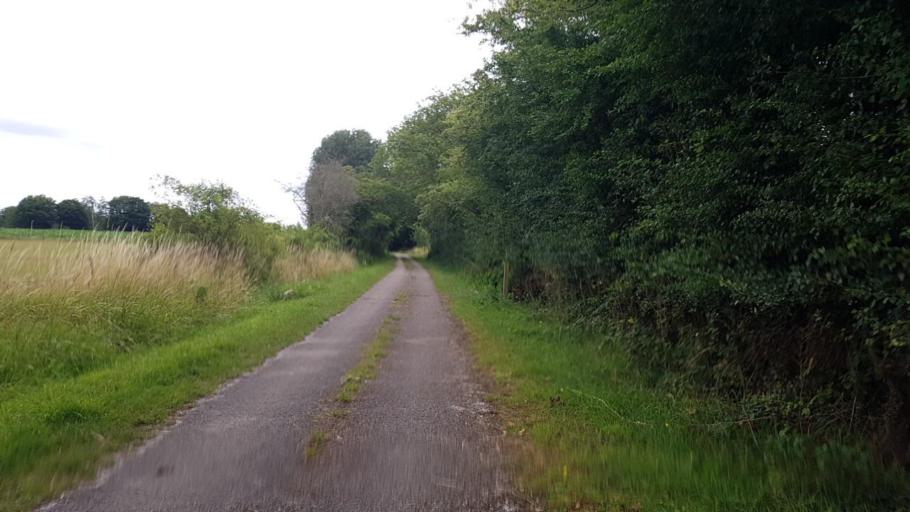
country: FR
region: Picardie
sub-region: Departement de l'Aisne
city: Buironfosse
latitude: 49.9023
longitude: 3.8156
